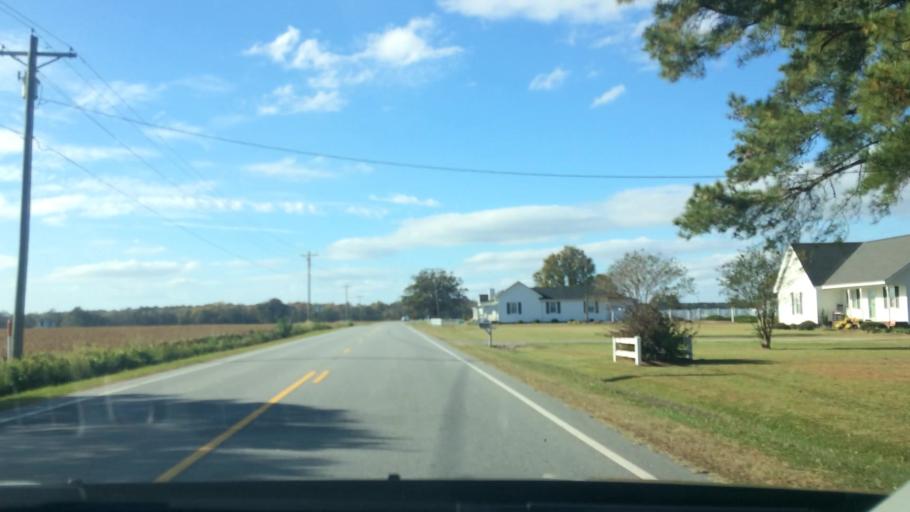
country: US
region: North Carolina
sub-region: Greene County
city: Maury
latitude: 35.4745
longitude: -77.5543
